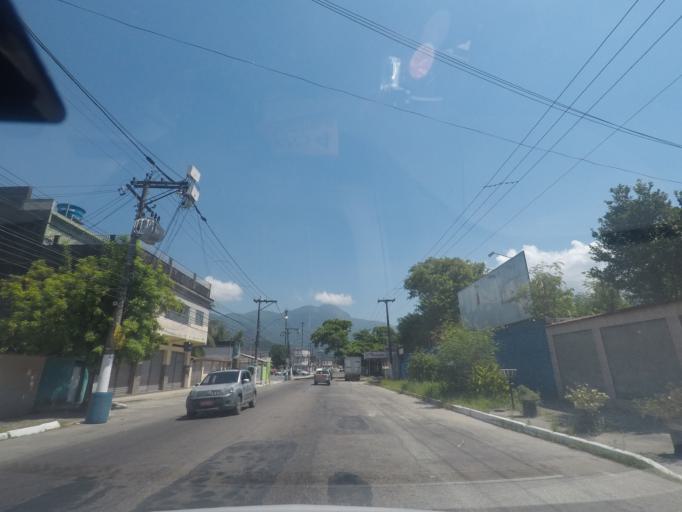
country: BR
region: Rio de Janeiro
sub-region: Petropolis
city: Petropolis
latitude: -22.5981
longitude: -43.1873
